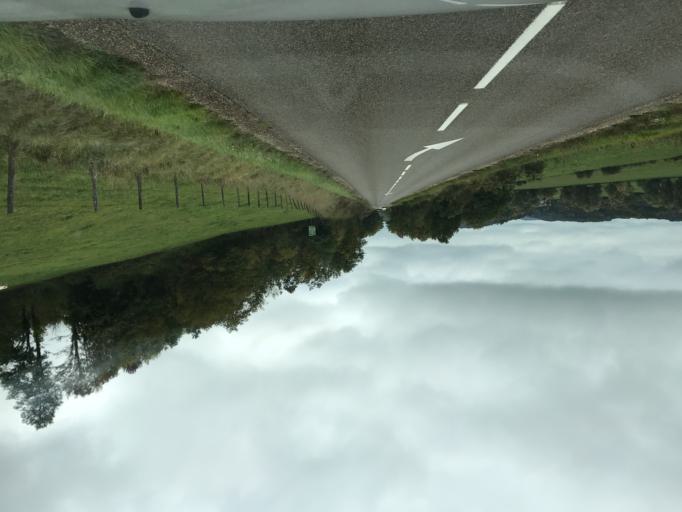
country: FR
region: Bourgogne
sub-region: Departement de Saone-et-Loire
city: Cuiseaux
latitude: 46.4161
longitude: 5.4531
